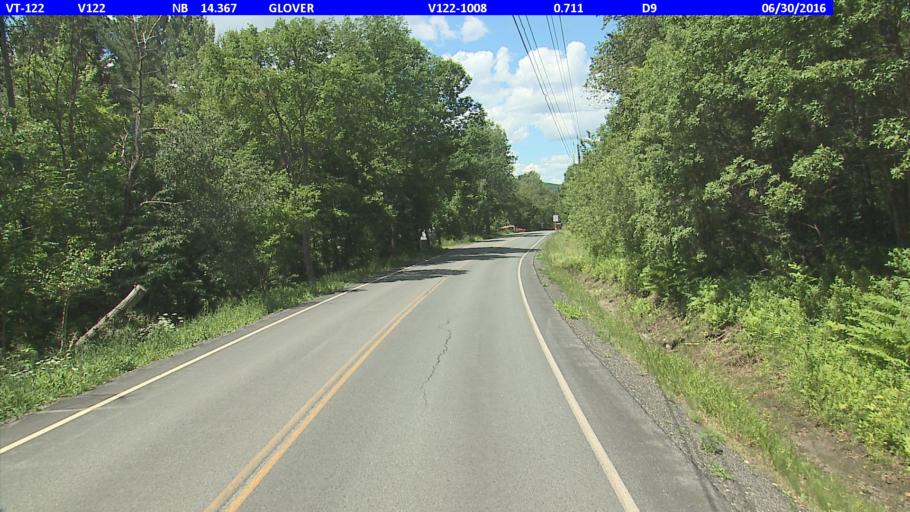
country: US
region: Vermont
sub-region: Caledonia County
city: Lyndonville
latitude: 44.6835
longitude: -72.1763
